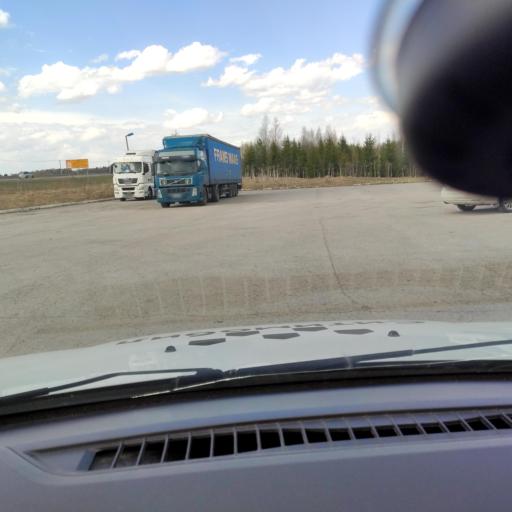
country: RU
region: Perm
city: Polazna
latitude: 58.2102
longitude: 56.4062
